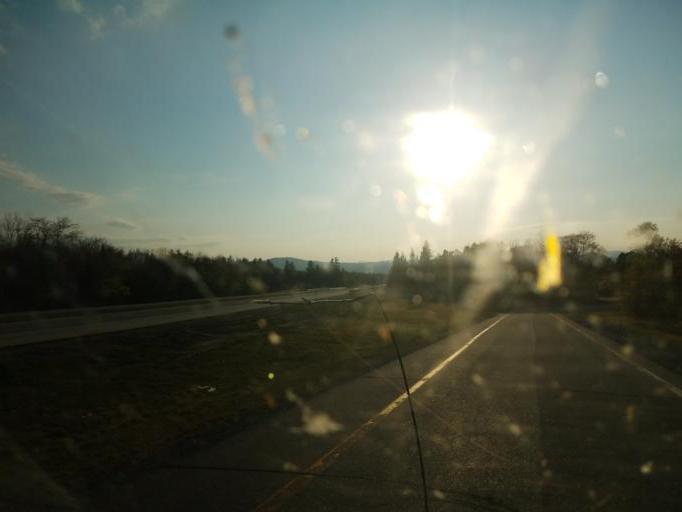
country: US
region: New Hampshire
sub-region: Grafton County
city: Deerfield
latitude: 44.2024
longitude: -71.6872
